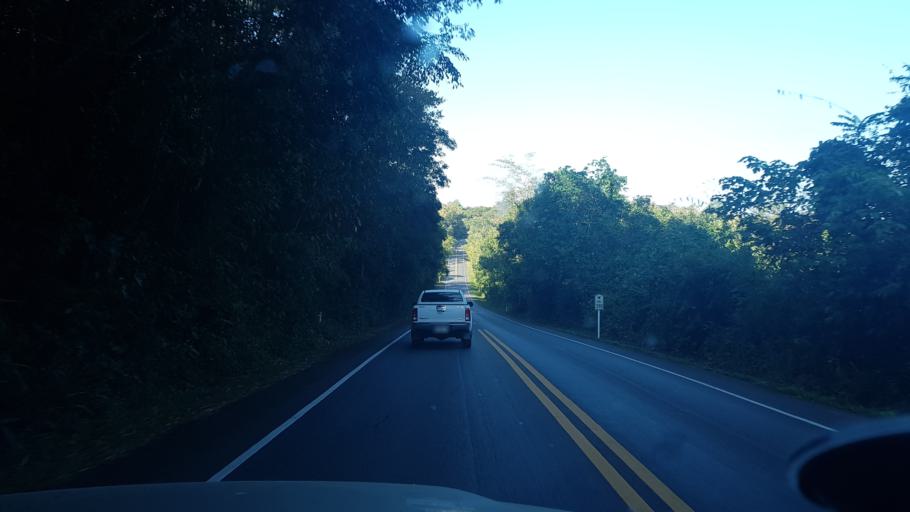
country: TH
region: Phetchabun
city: Nam Nao
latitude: 16.7613
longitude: 101.4798
